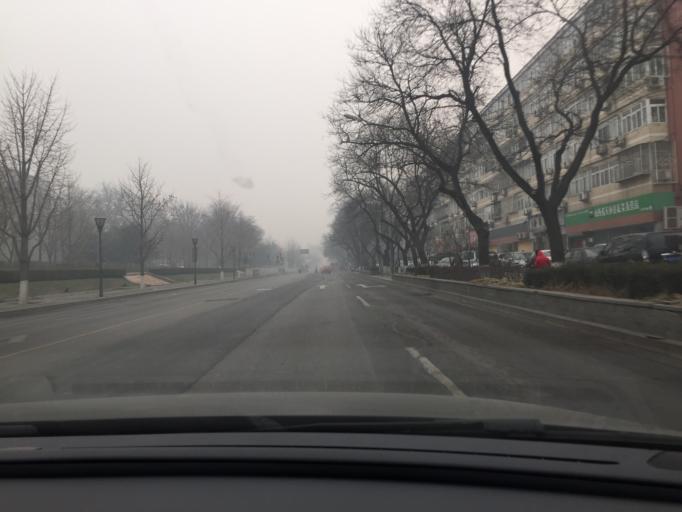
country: CN
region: Beijing
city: Jingshan
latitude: 39.9199
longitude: 116.4001
